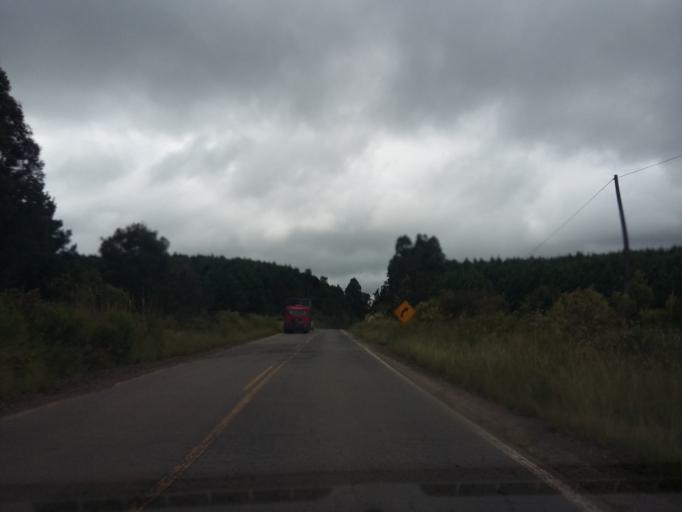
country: BR
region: Santa Catarina
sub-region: Lages
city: Lages
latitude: -27.8342
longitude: -50.2395
